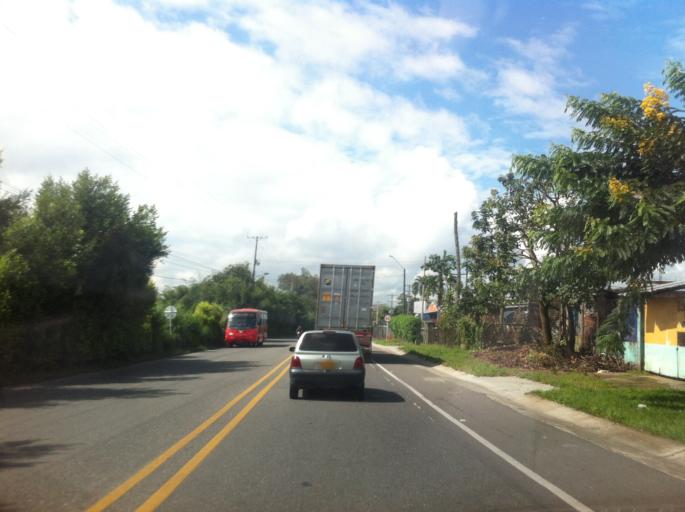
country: CO
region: Quindio
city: Armenia
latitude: 4.4967
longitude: -75.7311
